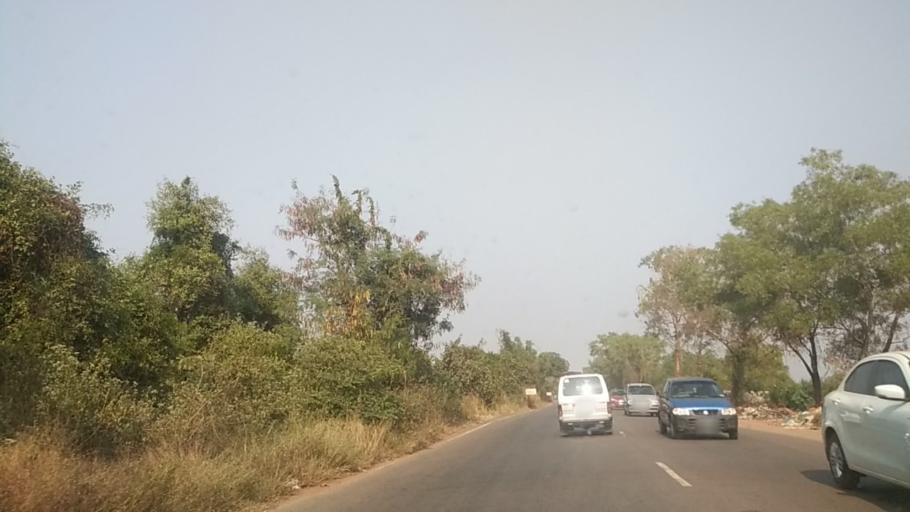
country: IN
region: Goa
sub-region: North Goa
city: Mapuca
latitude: 15.5837
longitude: 73.8163
